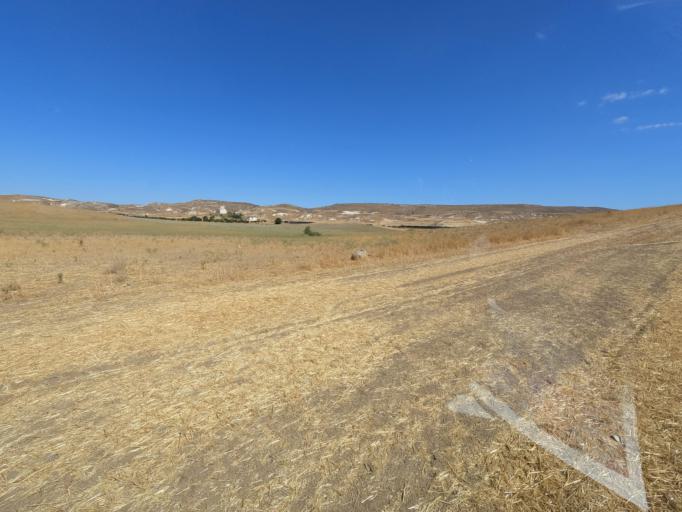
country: CY
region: Larnaka
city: Troulloi
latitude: 35.0244
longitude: 33.6008
